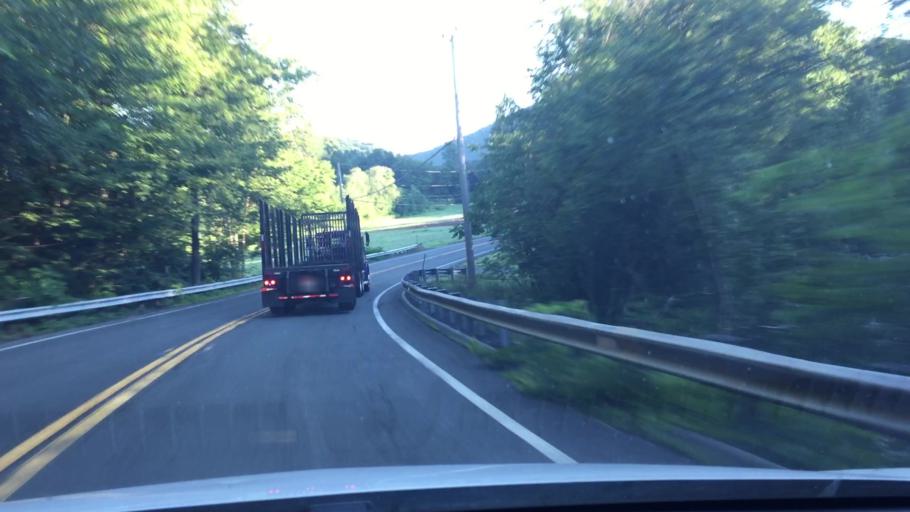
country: US
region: Massachusetts
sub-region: Berkshire County
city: Becket
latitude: 42.2631
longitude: -72.9629
